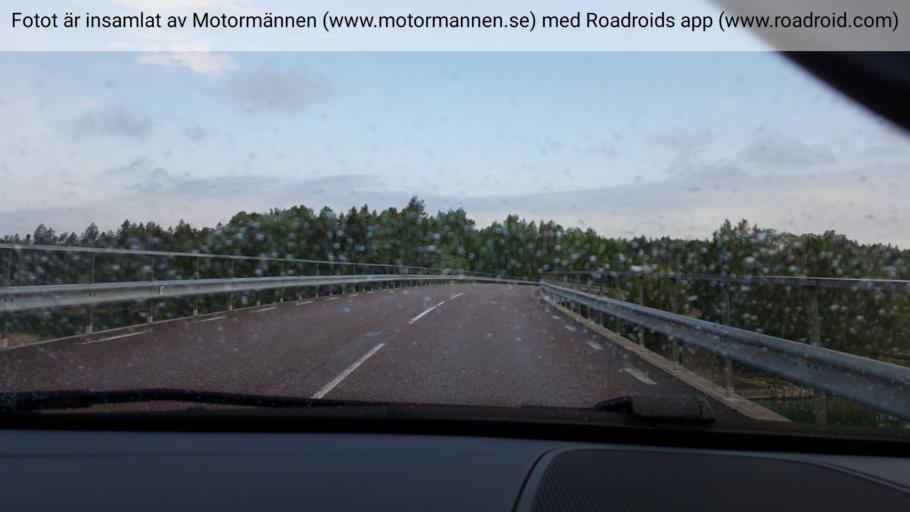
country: SE
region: Stockholm
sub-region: Nynashamns Kommun
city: Nynashamn
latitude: 58.9567
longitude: 17.9630
